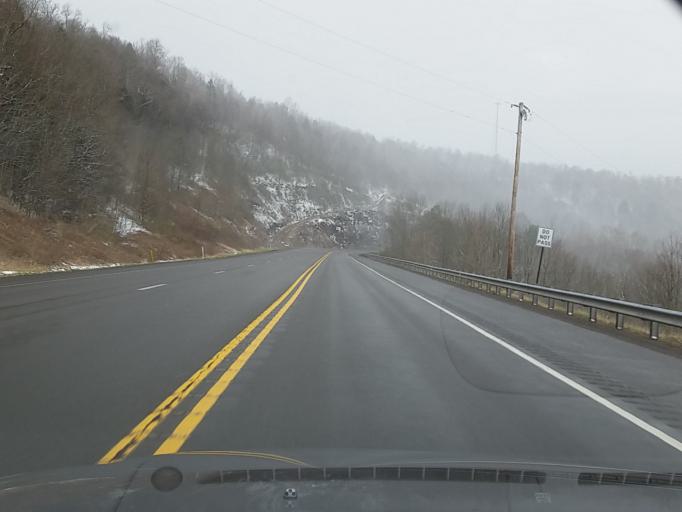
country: US
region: Pennsylvania
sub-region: Sullivan County
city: Laporte
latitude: 41.3630
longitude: -76.5392
